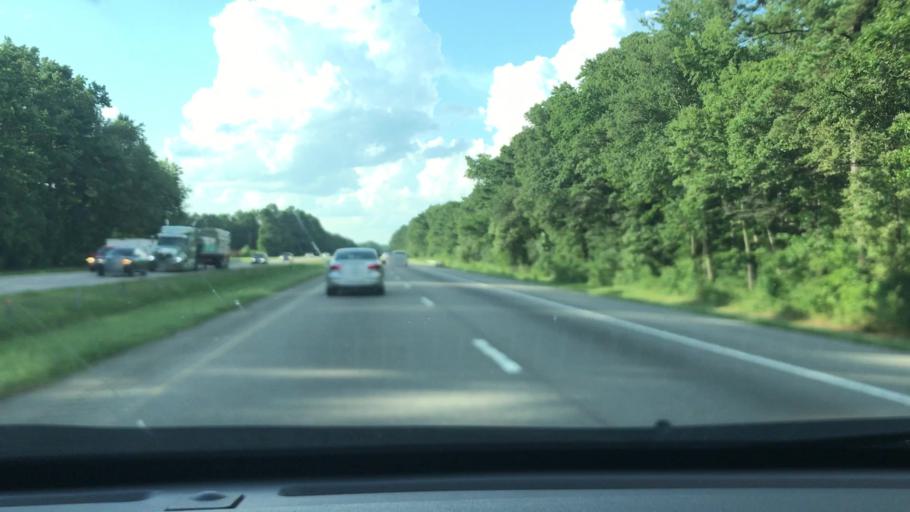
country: US
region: North Carolina
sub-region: Robeson County
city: Saint Pauls
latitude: 34.7526
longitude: -78.9970
